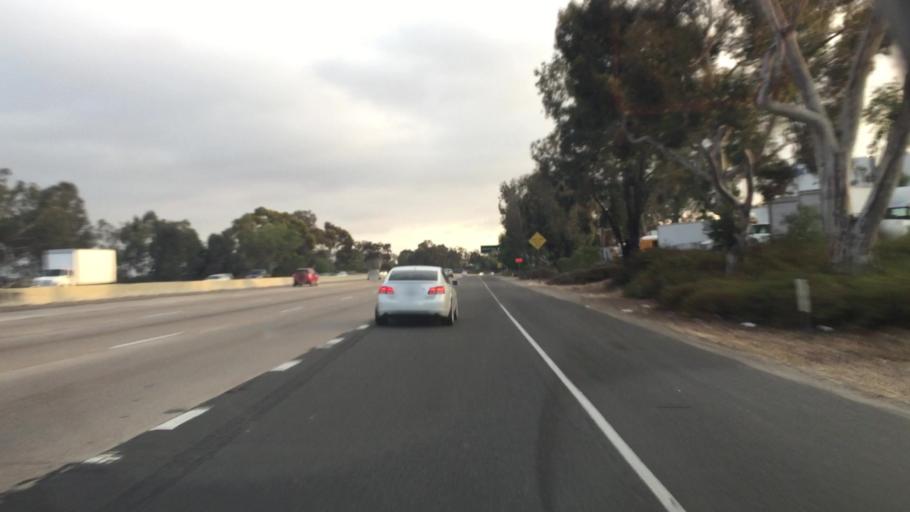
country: US
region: California
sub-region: San Diego County
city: National City
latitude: 32.7210
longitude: -117.0801
